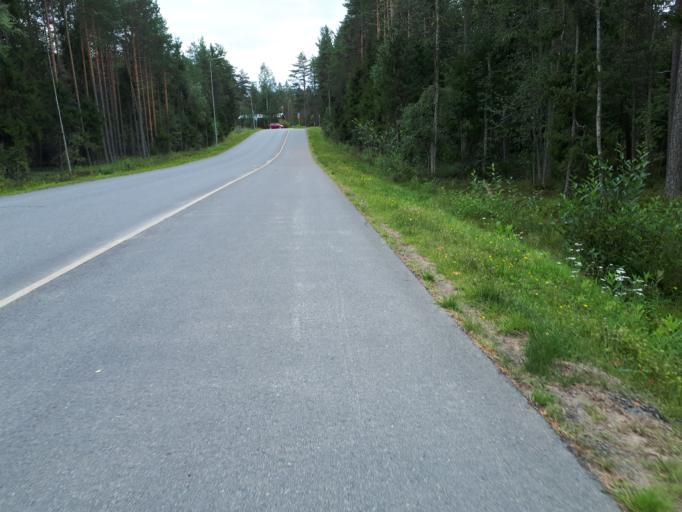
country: FI
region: Northern Ostrobothnia
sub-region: Oulunkaari
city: Ii
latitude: 65.3206
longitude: 25.4100
